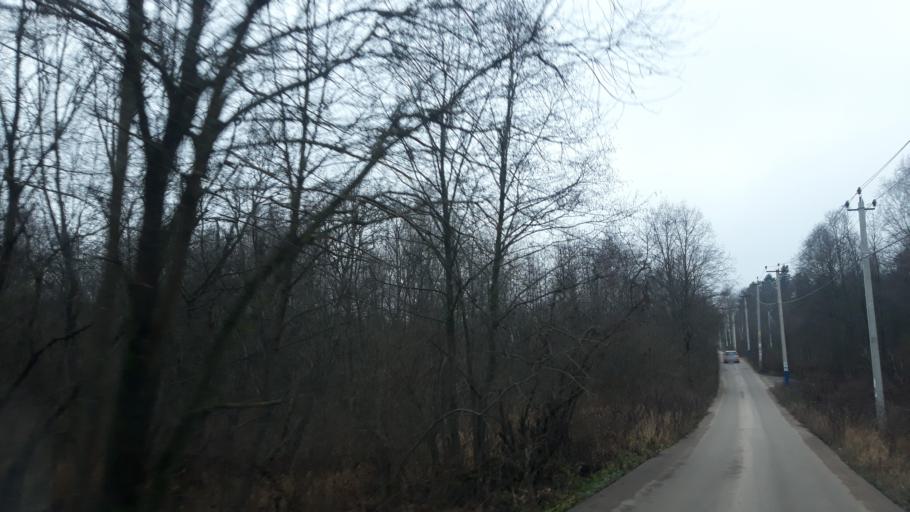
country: RU
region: Moskovskaya
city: Lozhki
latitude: 56.0655
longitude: 37.1104
